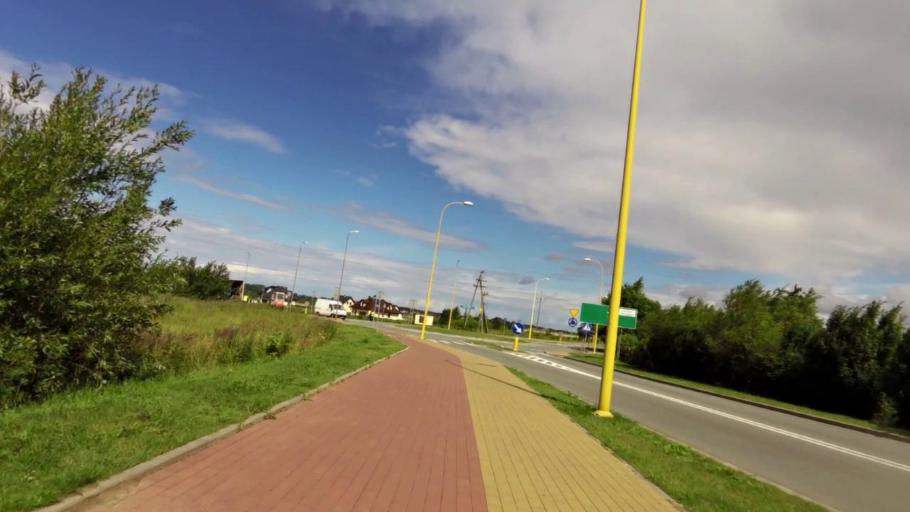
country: PL
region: West Pomeranian Voivodeship
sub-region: Powiat slawienski
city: Darlowo
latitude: 54.4275
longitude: 16.4155
